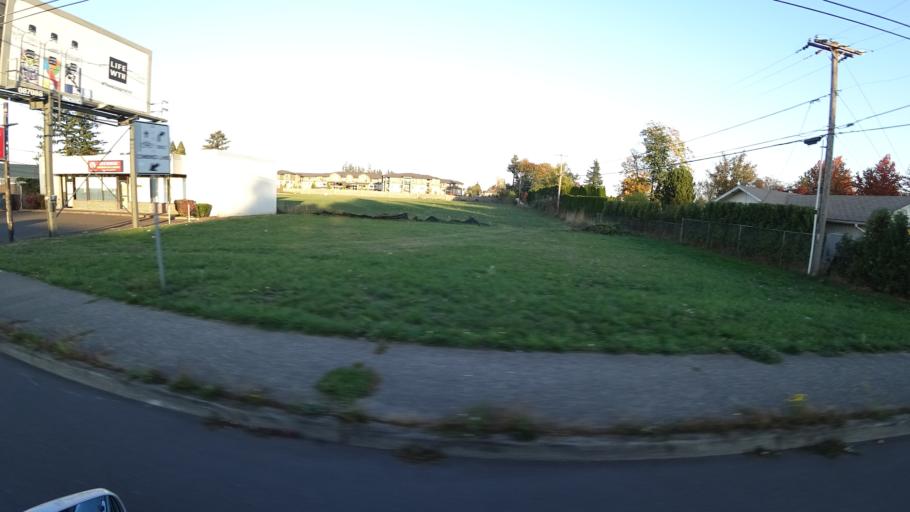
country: US
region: Oregon
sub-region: Multnomah County
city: Gresham
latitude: 45.5175
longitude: -122.4337
